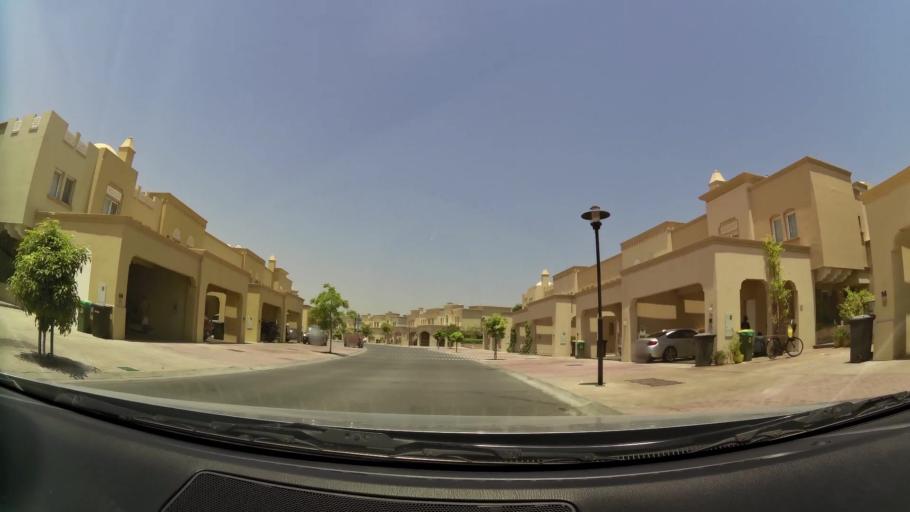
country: AE
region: Dubai
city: Dubai
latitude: 25.0561
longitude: 55.1781
